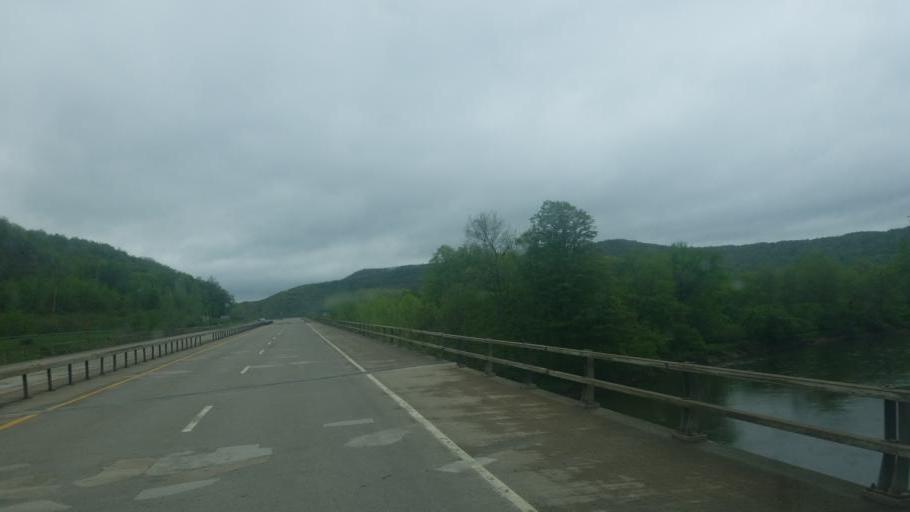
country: US
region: New York
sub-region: Cattaraugus County
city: Salamanca
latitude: 42.0857
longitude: -78.6330
